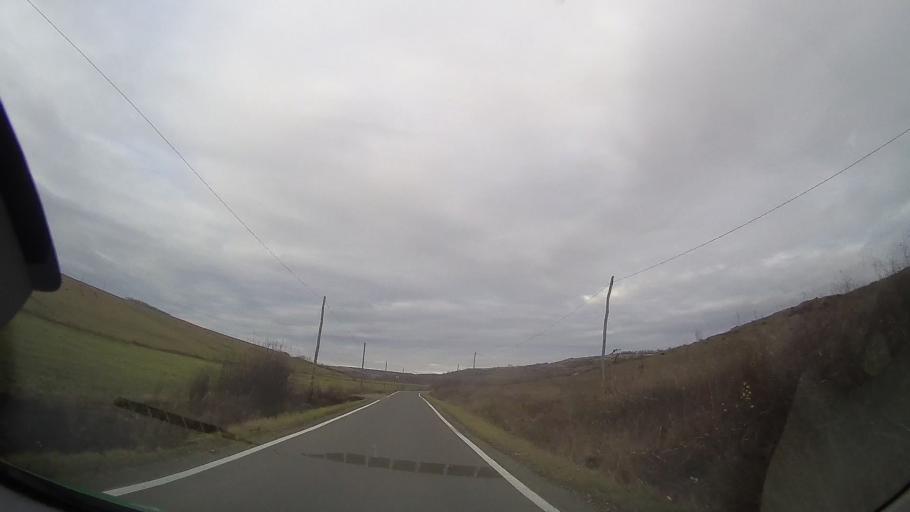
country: RO
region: Mures
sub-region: Comuna Cozma
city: Cozma
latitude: 46.7967
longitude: 24.5405
